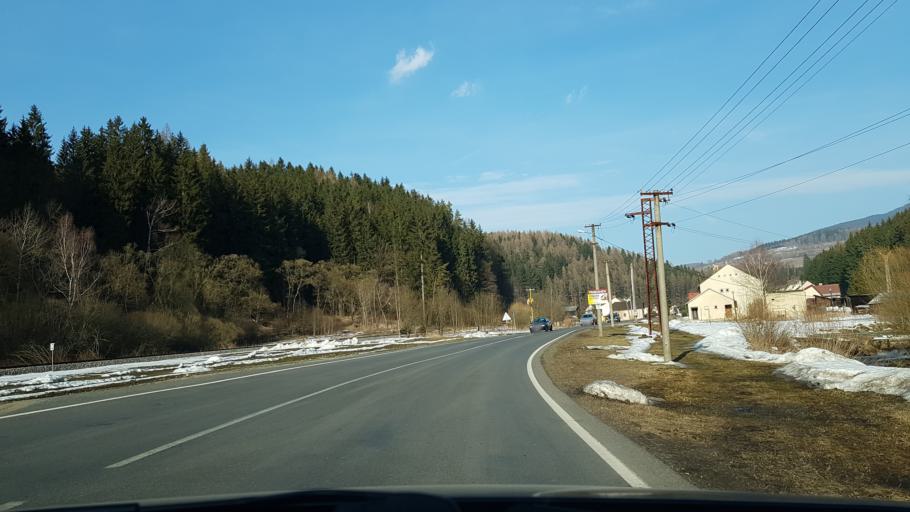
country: CZ
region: Olomoucky
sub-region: Okres Sumperk
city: Hanusovice
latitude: 50.1064
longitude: 16.9953
